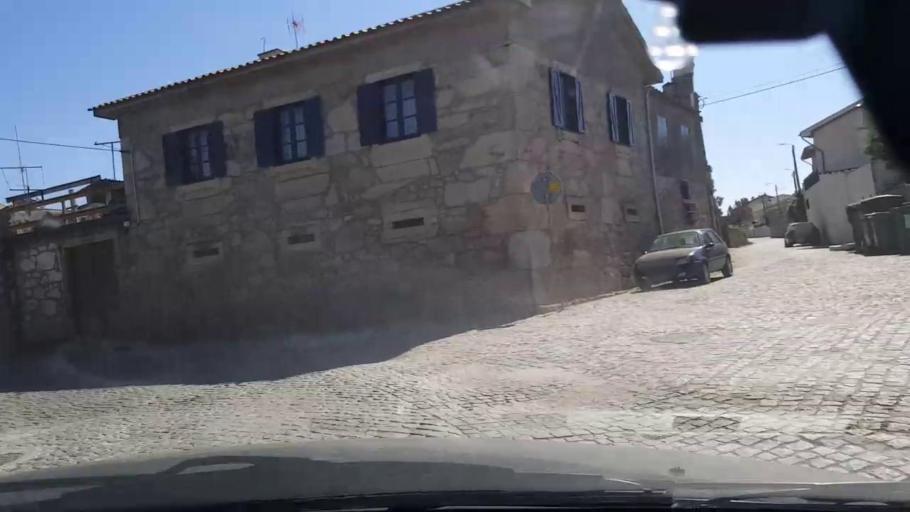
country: PT
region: Porto
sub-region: Vila do Conde
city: Arvore
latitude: 41.3214
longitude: -8.7015
